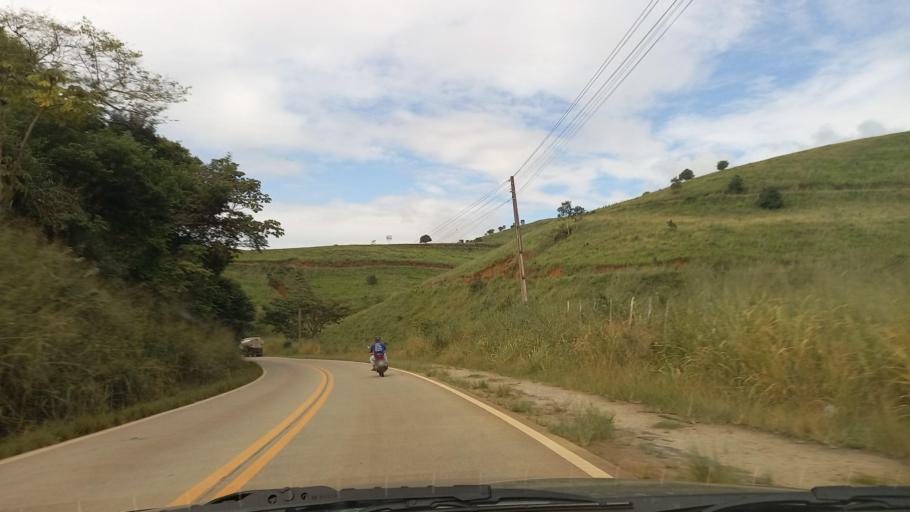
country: BR
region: Pernambuco
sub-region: Maraial
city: Maraial
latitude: -8.7462
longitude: -35.8030
